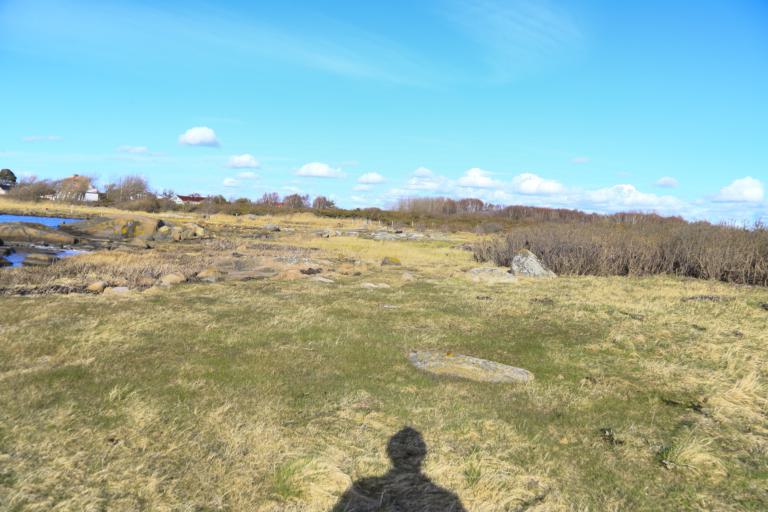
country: SE
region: Halland
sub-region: Varbergs Kommun
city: Varberg
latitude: 57.1237
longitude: 12.2025
